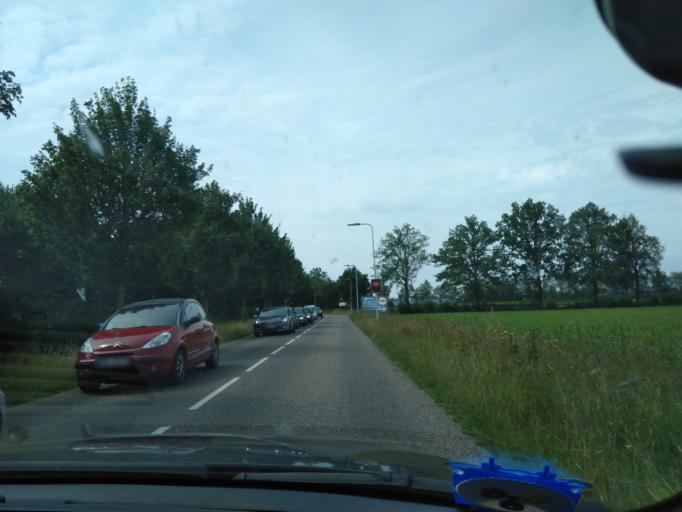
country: DE
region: Lower Saxony
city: Nordhorn
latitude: 52.3989
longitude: 7.0289
